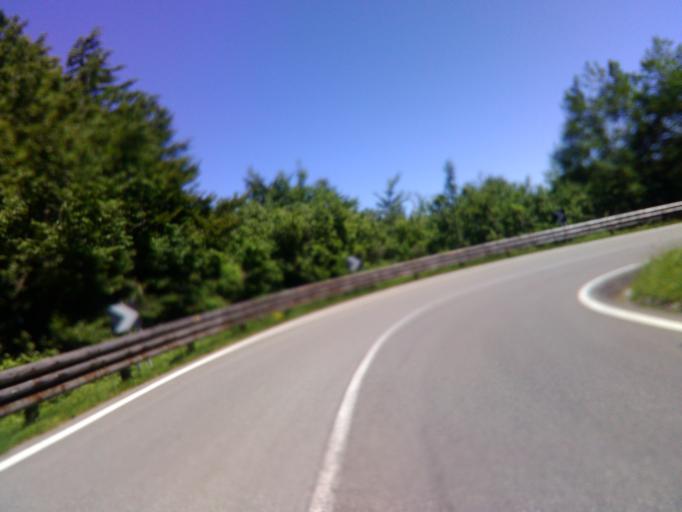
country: IT
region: Emilia-Romagna
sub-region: Provincia di Parma
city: Berceto
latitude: 44.4741
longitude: 9.9414
